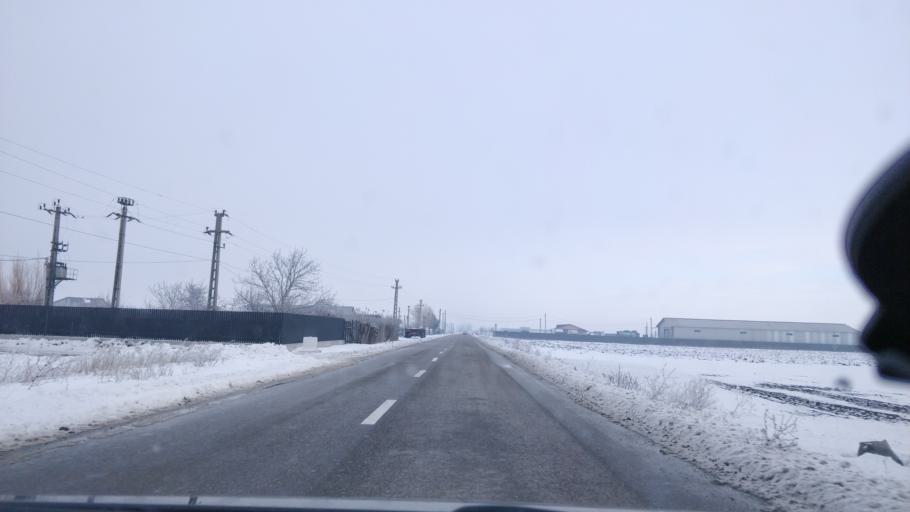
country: RO
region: Vrancea
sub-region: Comuna Vrancioaia
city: Focsani
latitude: 45.6978
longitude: 27.2166
